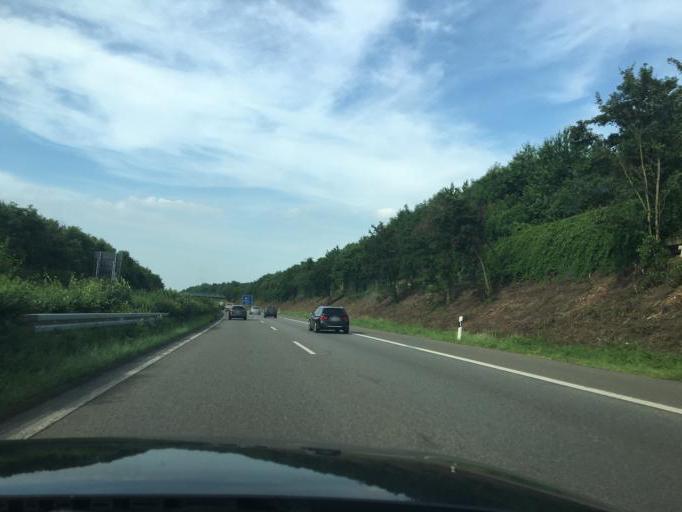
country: DE
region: North Rhine-Westphalia
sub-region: Regierungsbezirk Dusseldorf
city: Hochfeld
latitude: 51.3602
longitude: 6.7651
